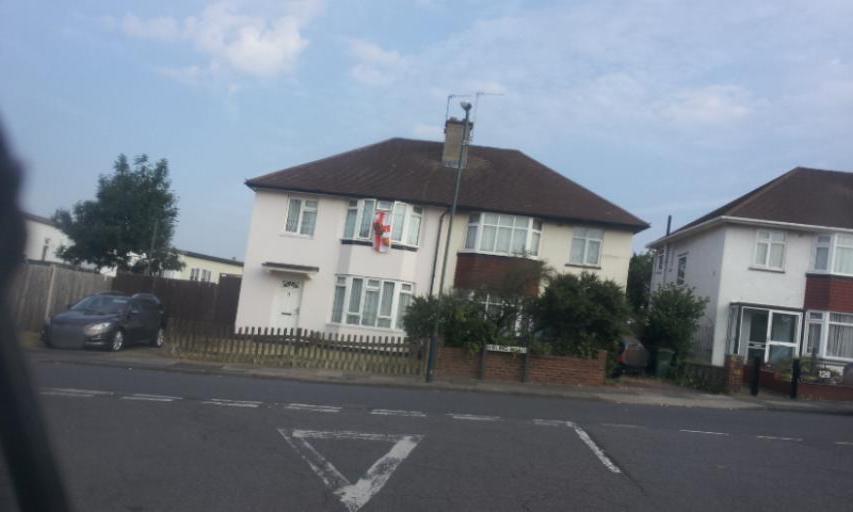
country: GB
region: England
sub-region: Greater London
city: Erith
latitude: 51.4719
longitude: 0.1752
